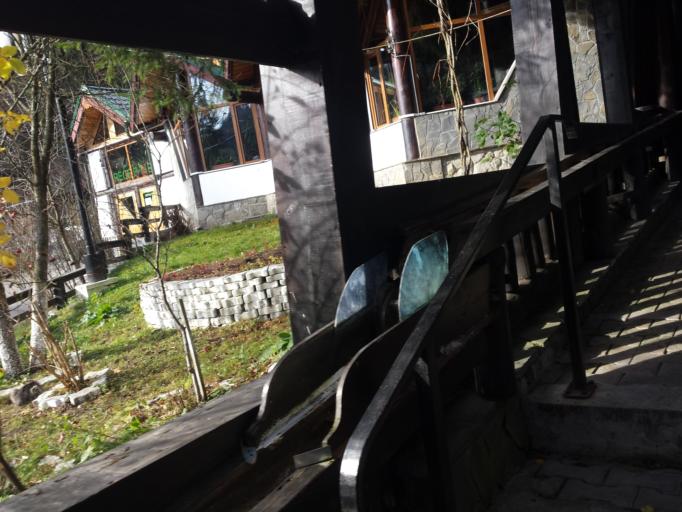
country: RO
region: Prahova
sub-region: Oras Azuga
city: Azuga
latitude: 45.4487
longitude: 25.5201
